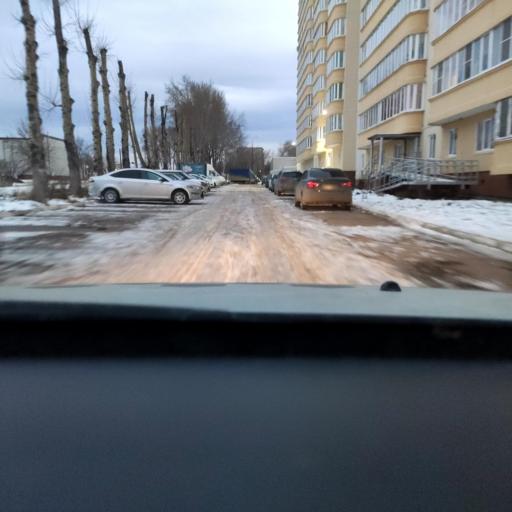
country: RU
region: Perm
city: Gamovo
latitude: 57.8715
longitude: 56.0967
